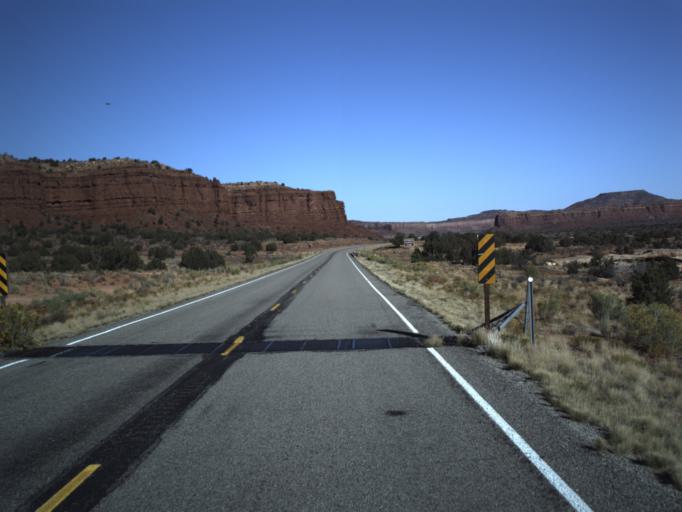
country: US
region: Utah
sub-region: San Juan County
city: Blanding
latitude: 37.6811
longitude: -110.2187
